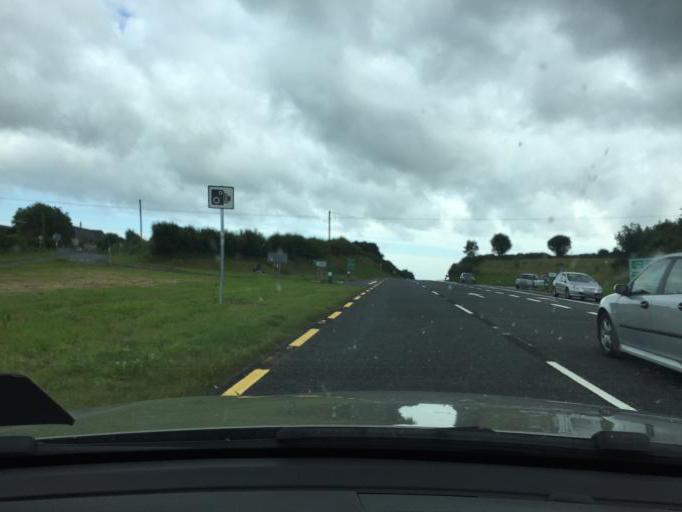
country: IE
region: Munster
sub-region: Waterford
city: Dungarvan
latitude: 52.1274
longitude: -7.5635
